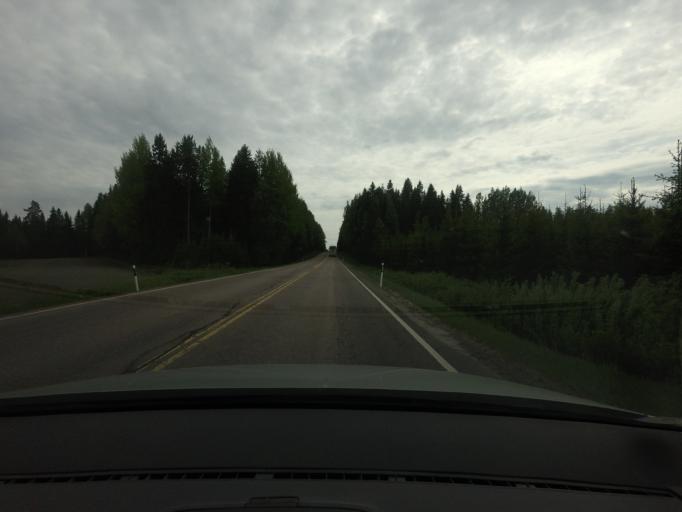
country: FI
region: Kymenlaakso
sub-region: Kotka-Hamina
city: Hamina
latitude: 60.6883
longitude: 27.2819
